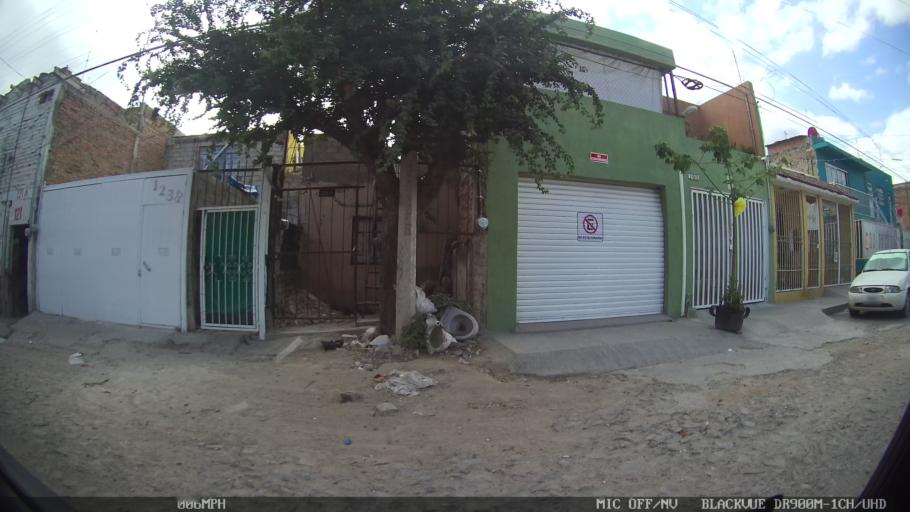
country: MX
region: Jalisco
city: Tlaquepaque
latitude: 20.6776
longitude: -103.2561
